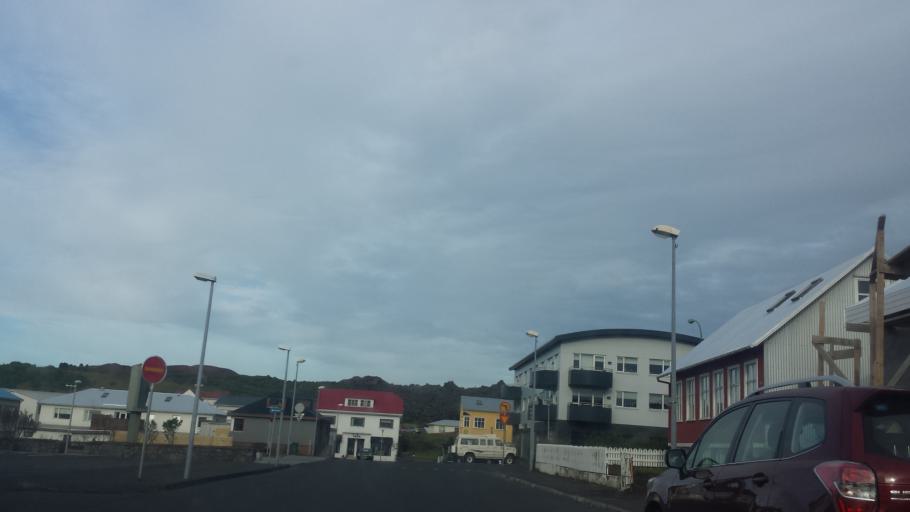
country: IS
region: South
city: Vestmannaeyjar
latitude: 63.4412
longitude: -20.2716
